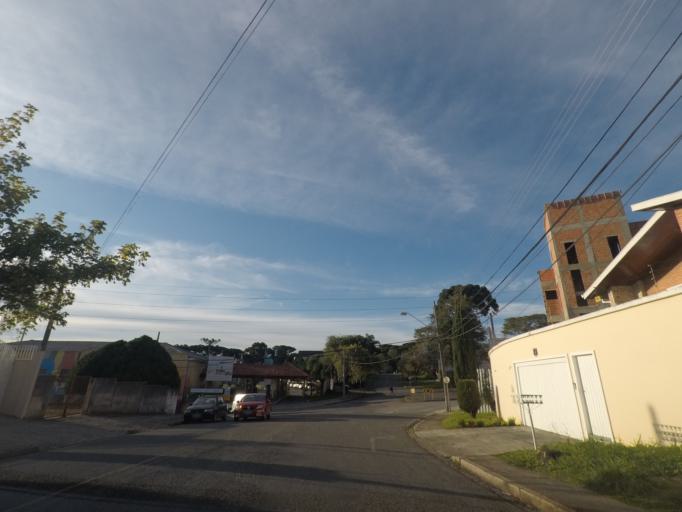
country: BR
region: Parana
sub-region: Curitiba
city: Curitiba
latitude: -25.4055
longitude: -49.2670
